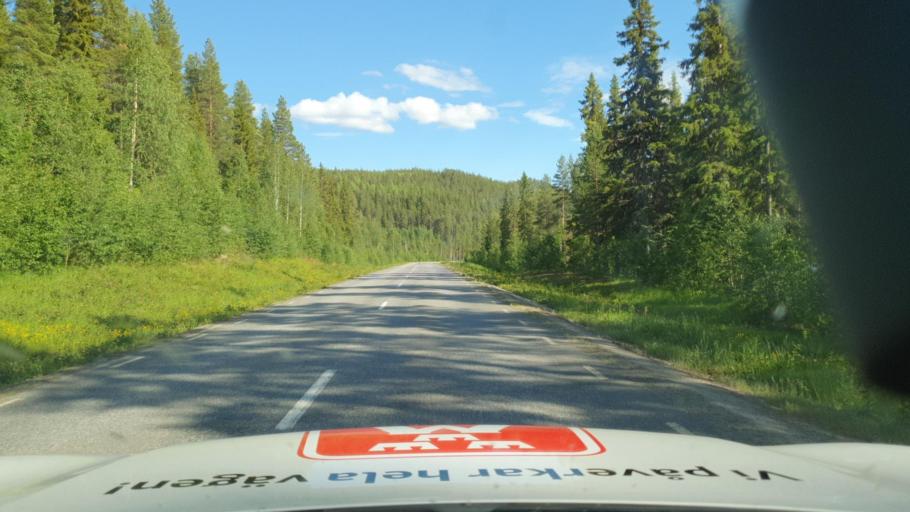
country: SE
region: Vaesterbotten
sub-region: Norsjo Kommun
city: Norsjoe
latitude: 64.8549
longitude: 19.7416
